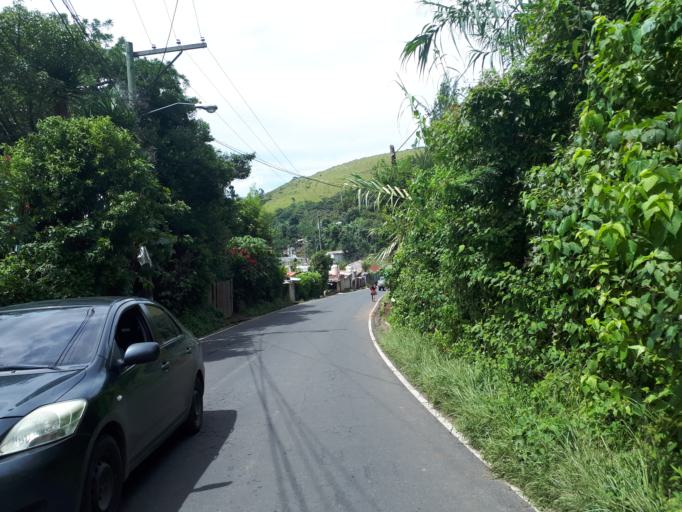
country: GT
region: Guatemala
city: Villa Canales
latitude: 14.4586
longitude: -90.5100
